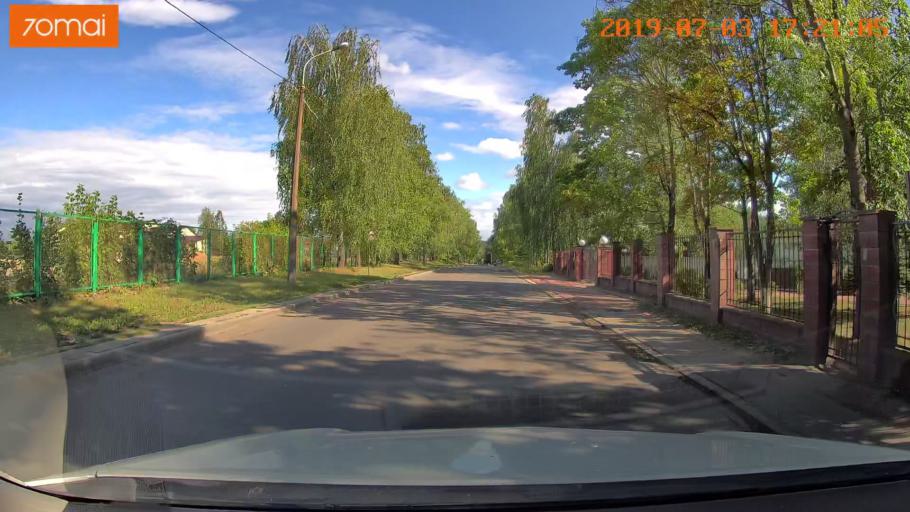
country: BY
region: Minsk
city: Vyaliki Trastsyanets
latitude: 53.9046
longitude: 27.6789
